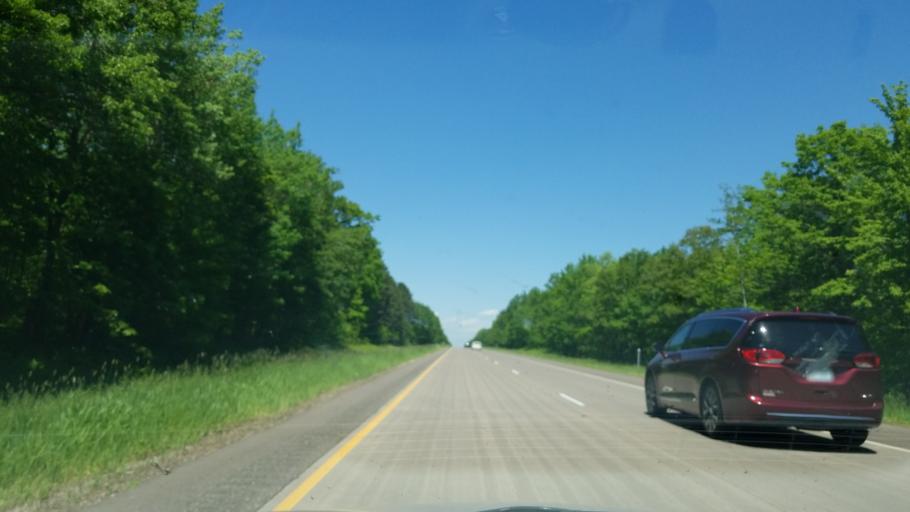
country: US
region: Minnesota
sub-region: Pine County
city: Hinckley
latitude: 46.0682
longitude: -92.9050
